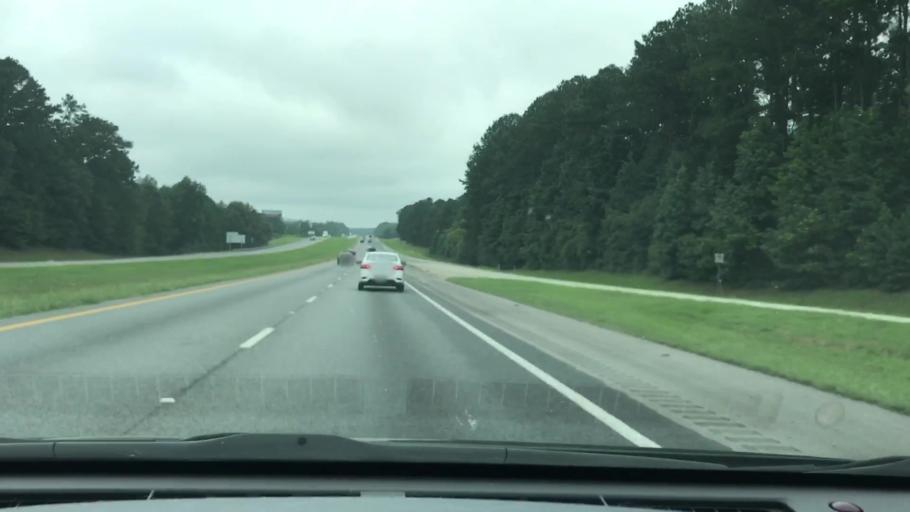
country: US
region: Georgia
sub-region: Walton County
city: Social Circle
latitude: 33.5943
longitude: -83.6333
